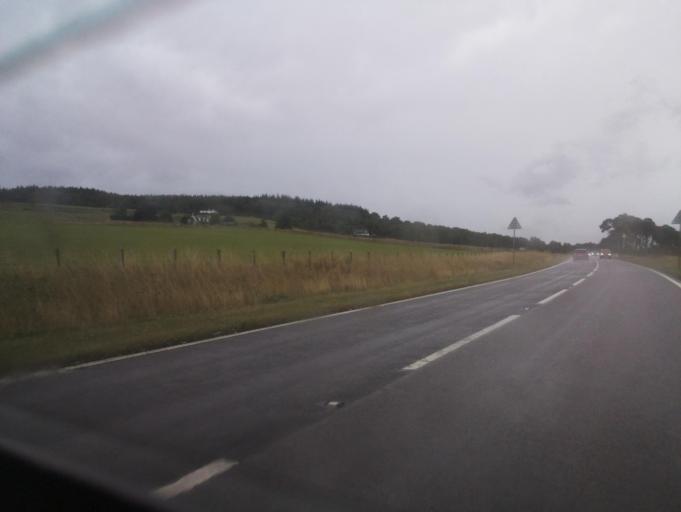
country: GB
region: Scotland
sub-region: Highland
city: Grantown on Spey
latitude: 57.2759
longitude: -3.7136
